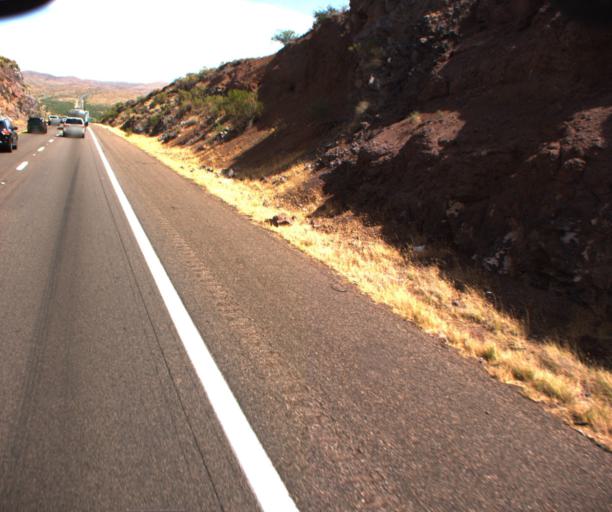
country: US
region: Arizona
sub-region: Yavapai County
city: Cordes Lakes
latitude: 34.2262
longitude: -112.1109
